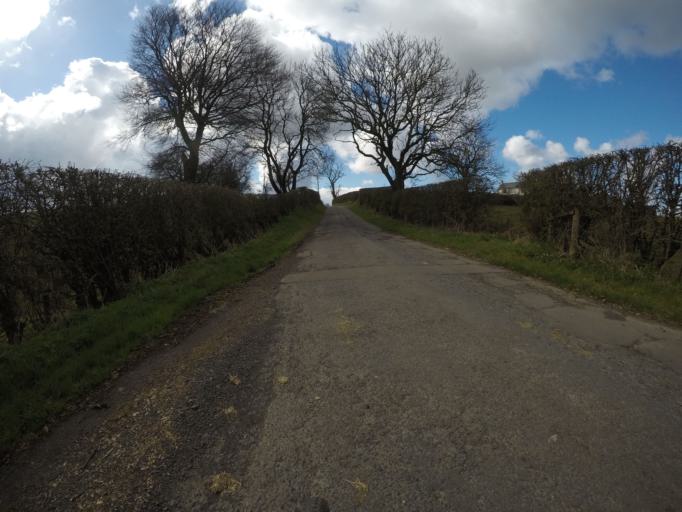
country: GB
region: Scotland
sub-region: North Ayrshire
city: Kilbirnie
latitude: 55.7234
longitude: -4.6661
